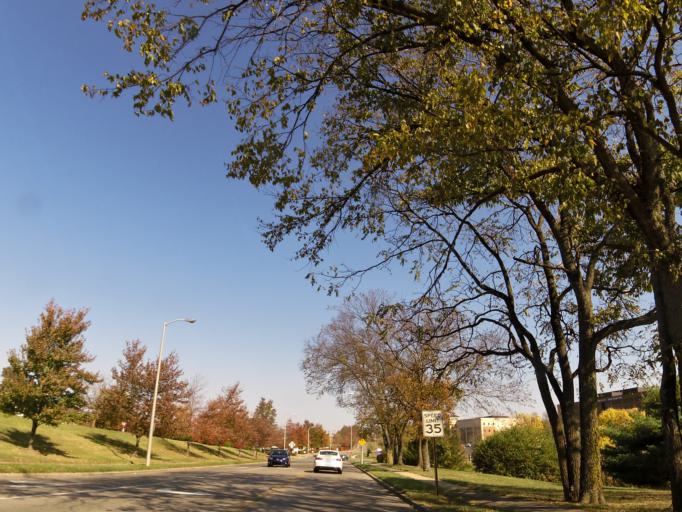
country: US
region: Kentucky
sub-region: Fayette County
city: Lexington
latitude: 37.9983
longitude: -84.4424
